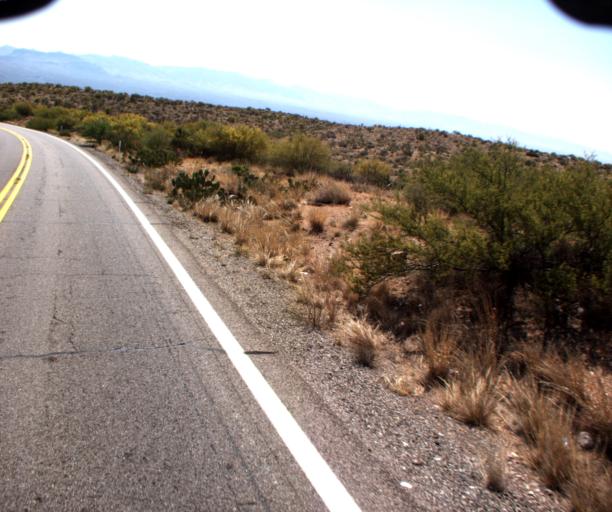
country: US
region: Arizona
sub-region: Pinal County
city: Mammoth
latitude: 32.6606
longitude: -110.6894
